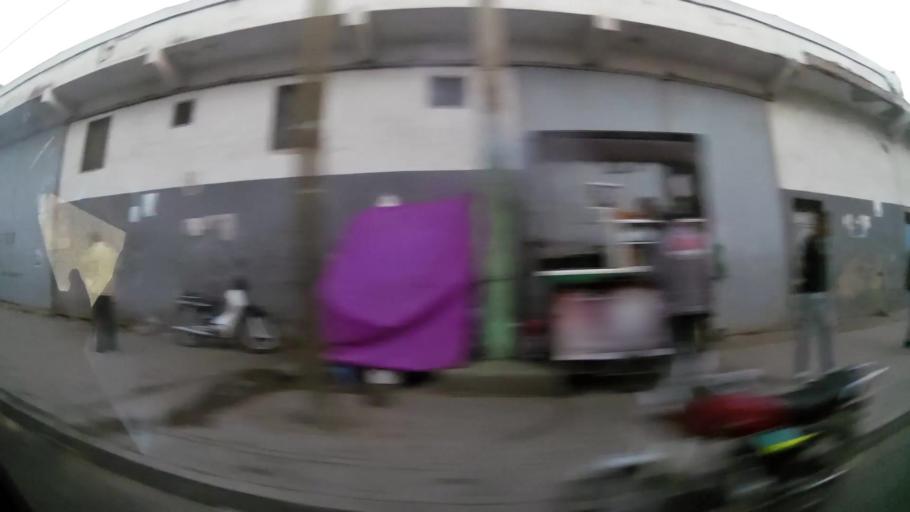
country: MA
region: Souss-Massa-Draa
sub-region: Inezgane-Ait Mellou
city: Inezgane
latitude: 30.3750
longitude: -9.4913
